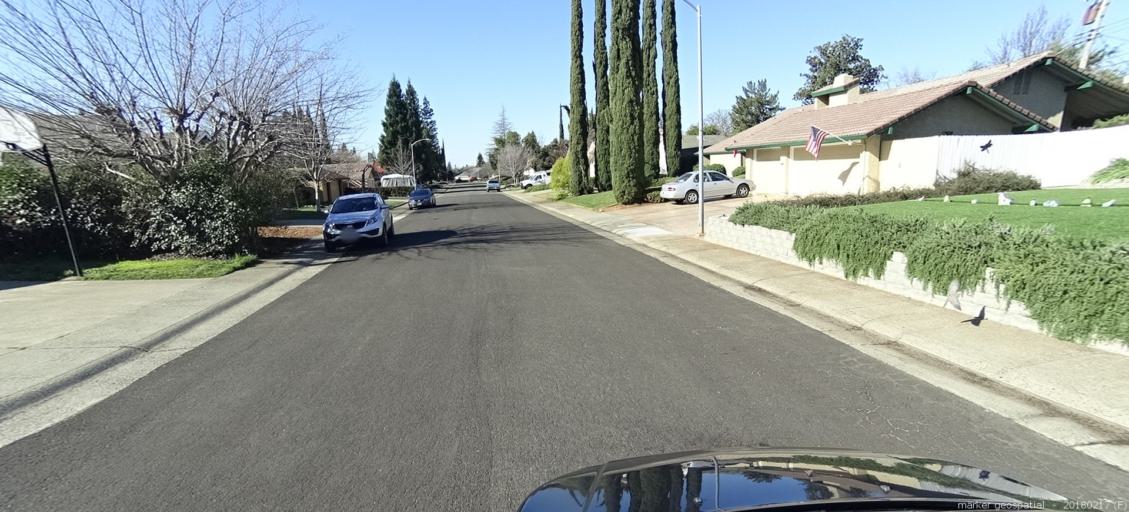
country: US
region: California
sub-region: Sacramento County
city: Folsom
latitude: 38.6607
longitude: -121.1980
